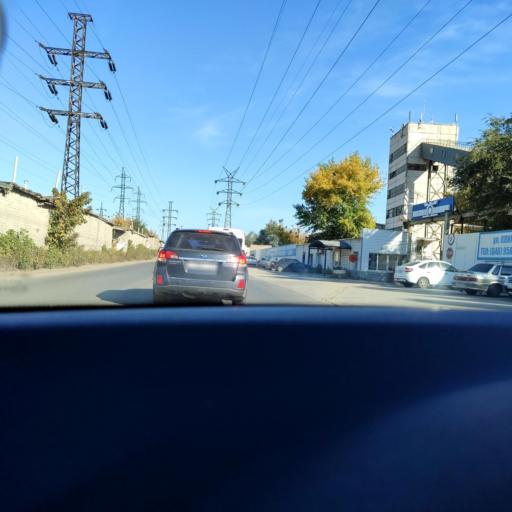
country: RU
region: Samara
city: Petra-Dubrava
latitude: 53.2491
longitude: 50.2937
